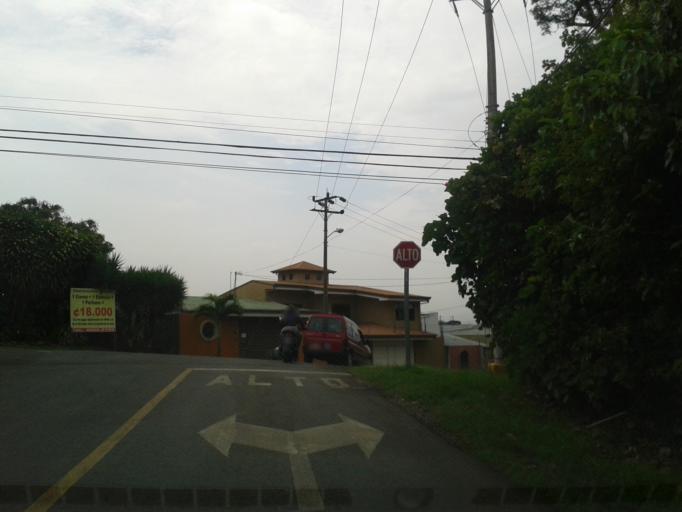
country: CR
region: Heredia
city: San Pablo
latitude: 9.9816
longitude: -84.1022
